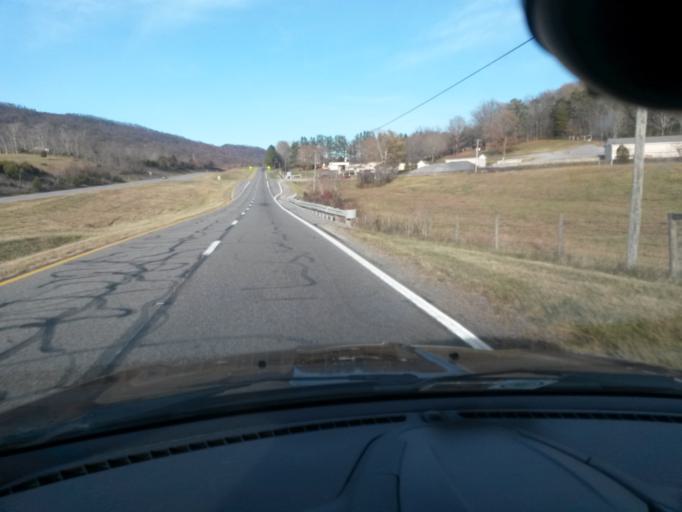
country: US
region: Virginia
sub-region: Botetourt County
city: Fincastle
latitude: 37.6111
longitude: -79.8317
